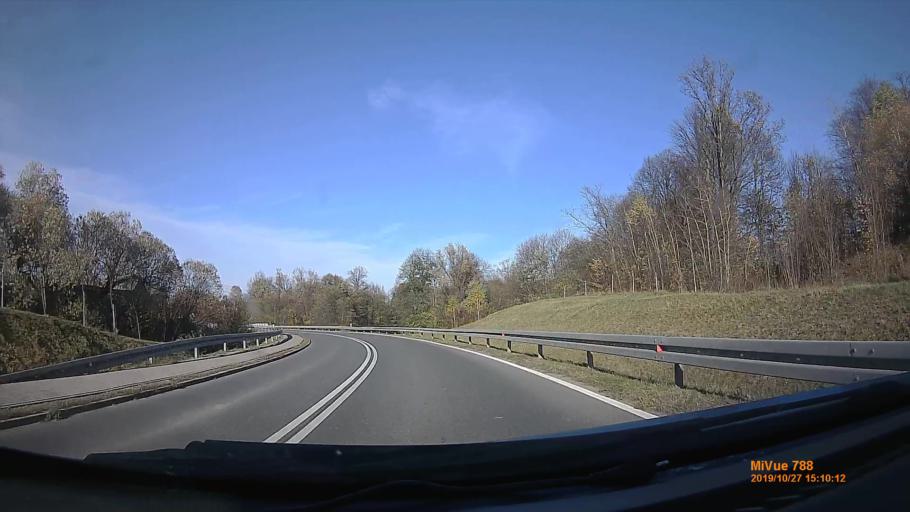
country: PL
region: Lower Silesian Voivodeship
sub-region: Powiat klodzki
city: Miedzylesie
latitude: 50.1860
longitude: 16.6713
